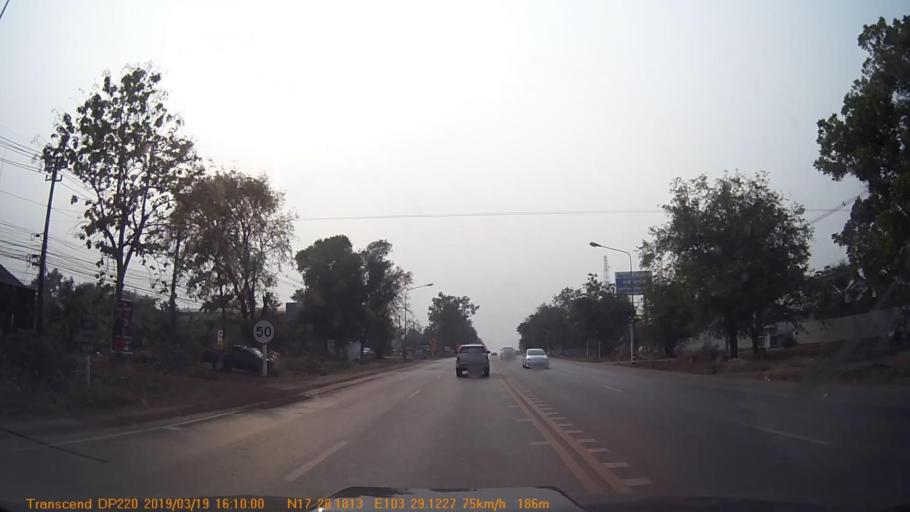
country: TH
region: Sakon Nakhon
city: Sawang Daen Din
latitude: 17.4697
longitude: 103.4851
